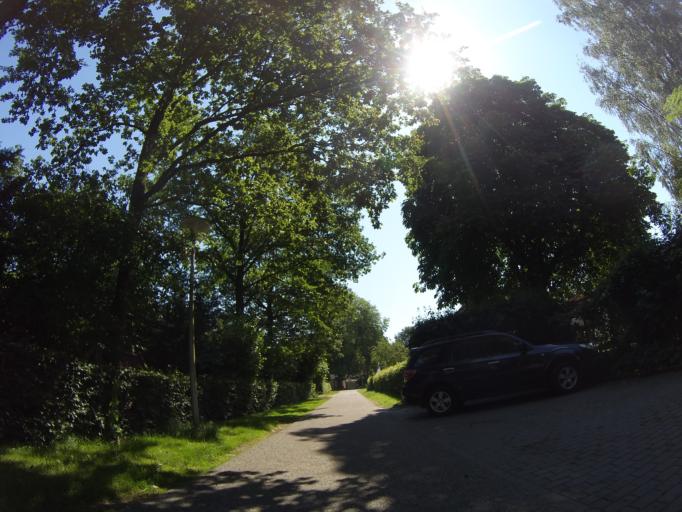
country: NL
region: Drenthe
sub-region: Gemeente Coevorden
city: Sleen
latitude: 52.7948
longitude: 6.7272
